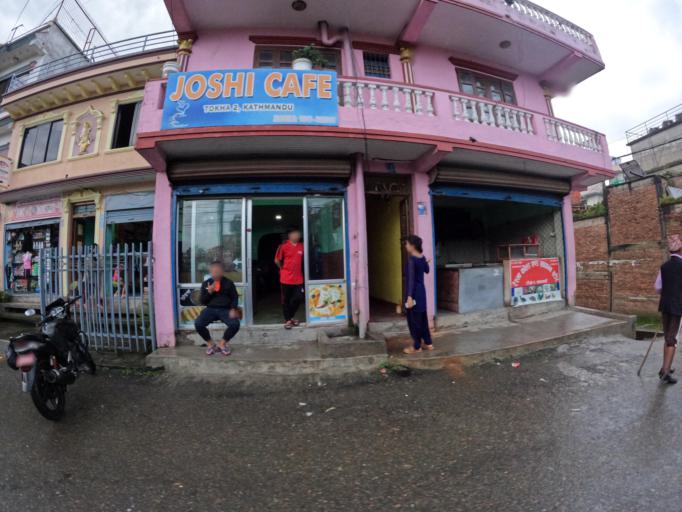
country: NP
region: Central Region
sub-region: Bagmati Zone
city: Kathmandu
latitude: 27.7691
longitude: 85.3304
